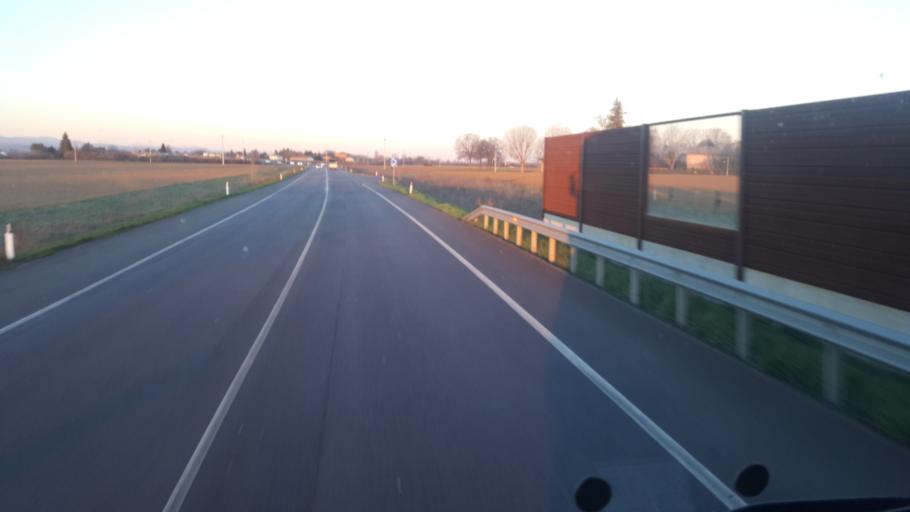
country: IT
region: Emilia-Romagna
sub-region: Provincia di Bologna
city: Crespellano
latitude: 44.5225
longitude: 11.1328
